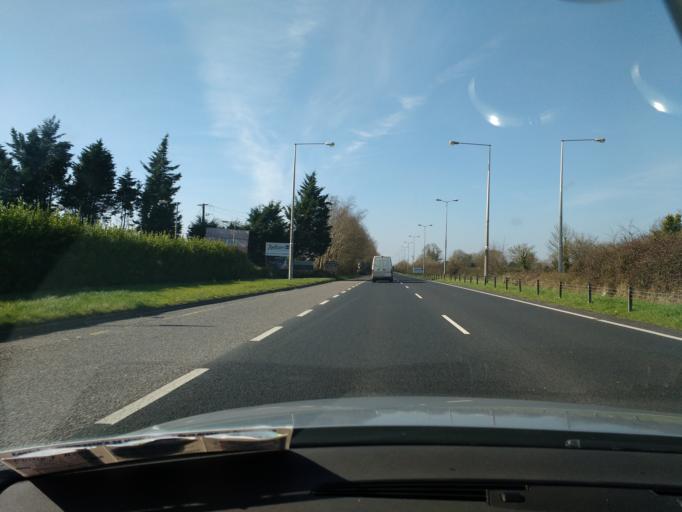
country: IE
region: Munster
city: Moyross
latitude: 52.6802
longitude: -8.7005
